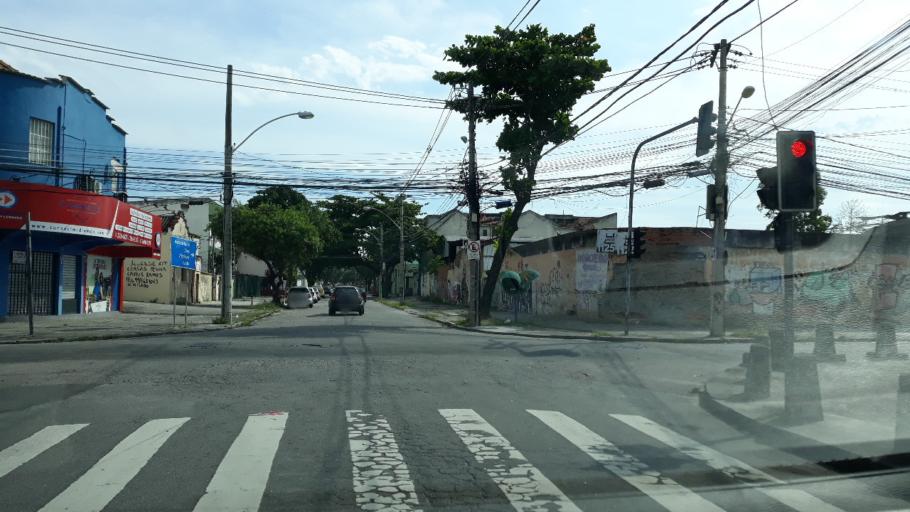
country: BR
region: Rio de Janeiro
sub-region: Duque De Caxias
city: Duque de Caxias
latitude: -22.8339
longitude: -43.2744
